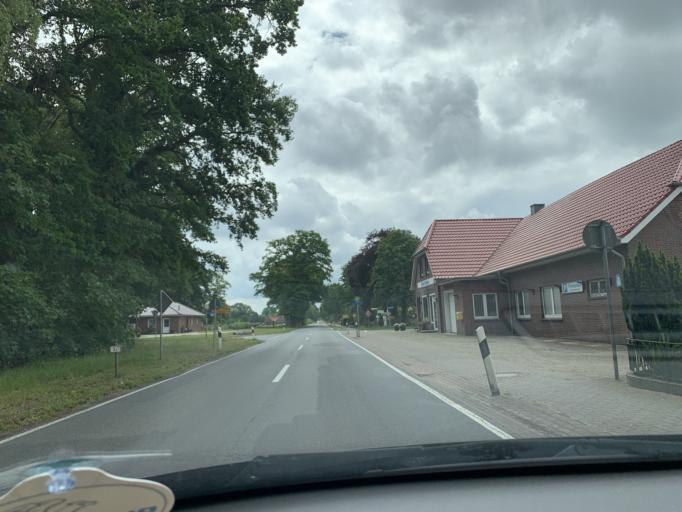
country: DE
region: Lower Saxony
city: Bockhorn
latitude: 53.3675
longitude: 8.0619
